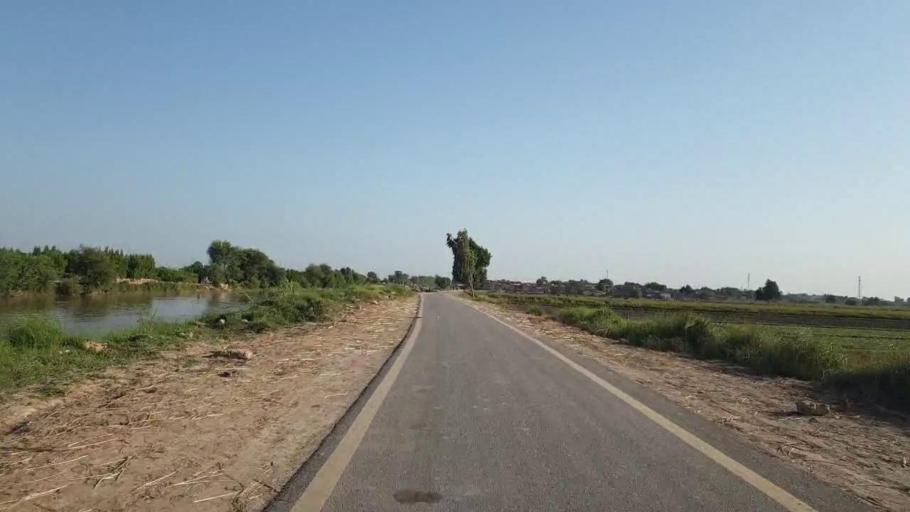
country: PK
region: Sindh
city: Hyderabad
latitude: 25.3270
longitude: 68.4253
